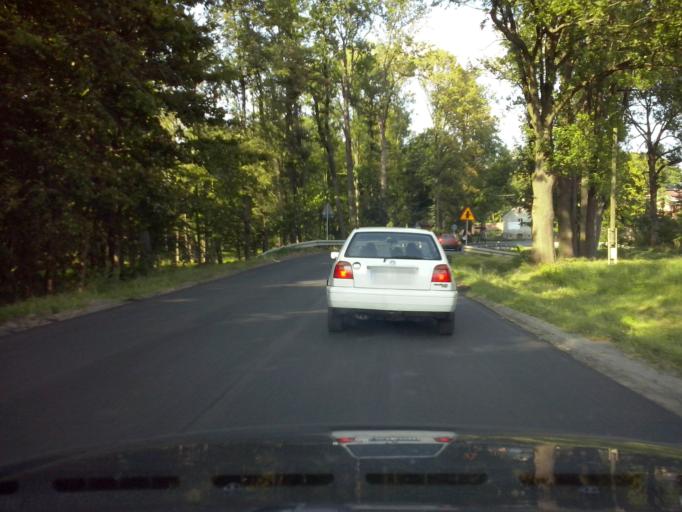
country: PL
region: Subcarpathian Voivodeship
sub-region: Powiat kolbuszowski
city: Kolbuszowa
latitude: 50.2538
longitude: 21.8083
